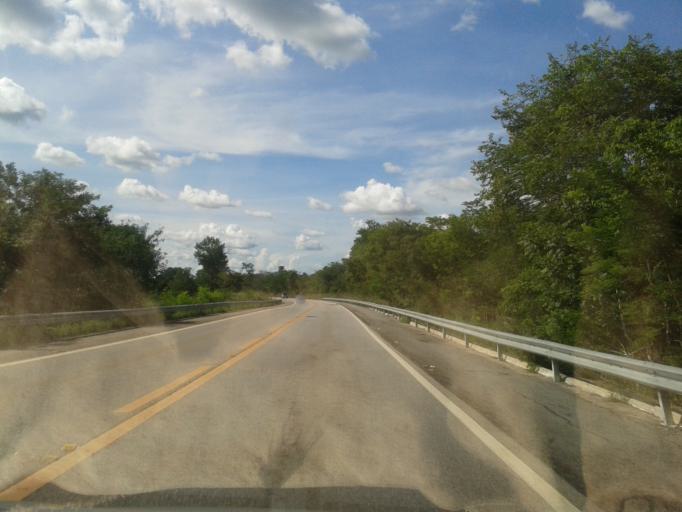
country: BR
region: Goias
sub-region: Mozarlandia
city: Mozarlandia
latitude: -15.1873
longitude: -50.5513
